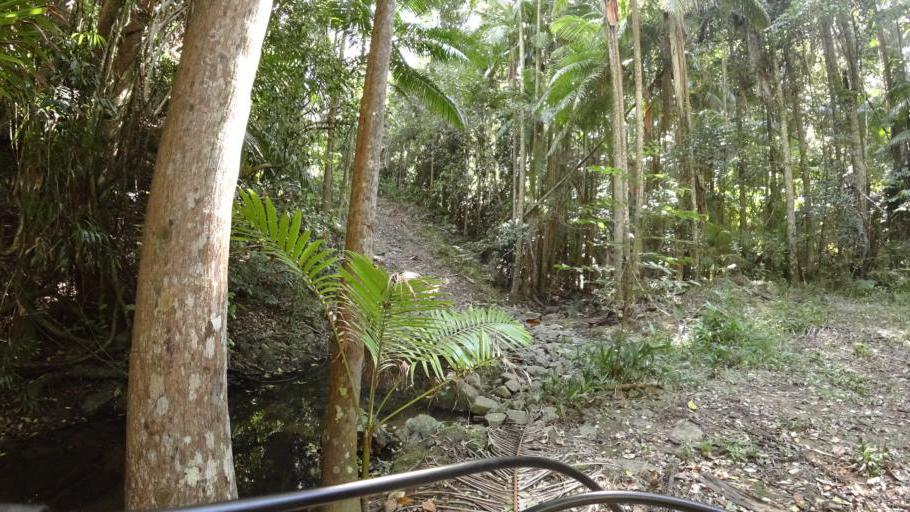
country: AU
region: Queensland
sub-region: Moreton Bay
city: Highvale
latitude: -27.4034
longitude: 152.7820
